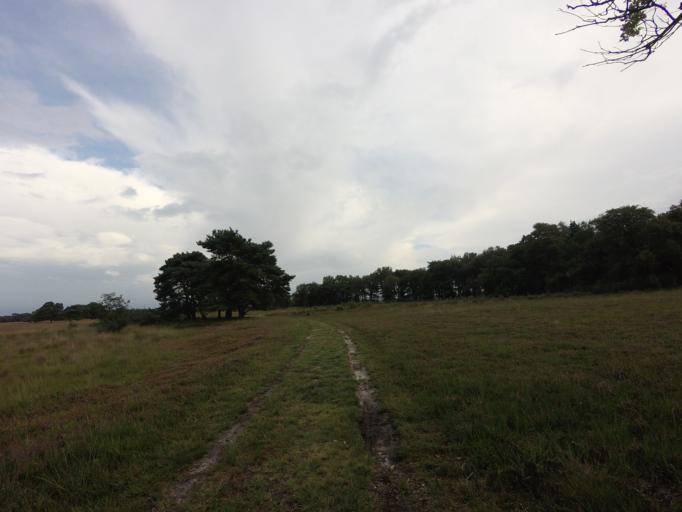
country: NL
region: Friesland
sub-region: Gemeente Heerenveen
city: Jubbega
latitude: 52.9590
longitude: 6.1373
